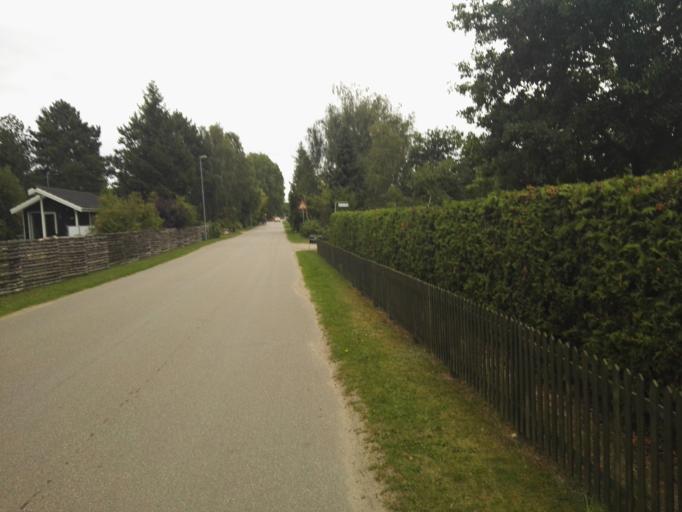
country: DK
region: Zealand
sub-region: Odsherred Kommune
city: Nykobing Sjaelland
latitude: 55.9350
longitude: 11.6667
